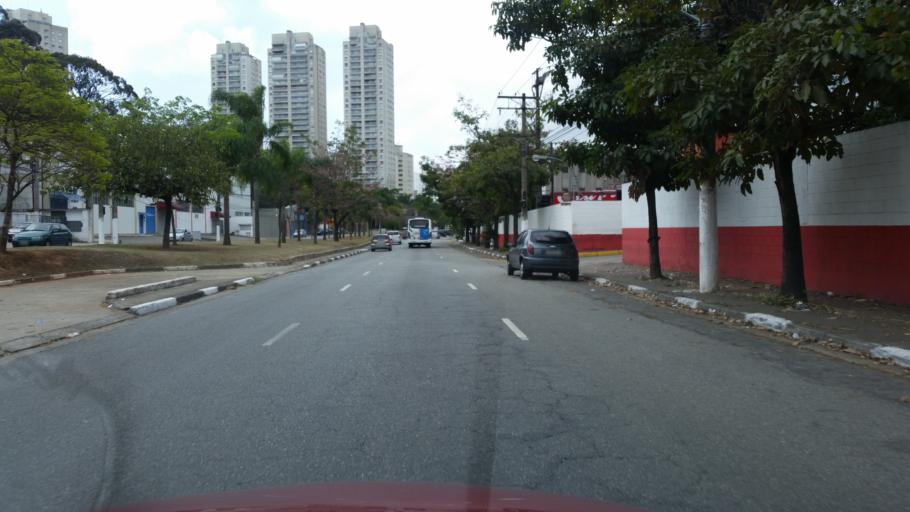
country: BR
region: Sao Paulo
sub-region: Diadema
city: Diadema
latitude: -23.6695
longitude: -46.6958
